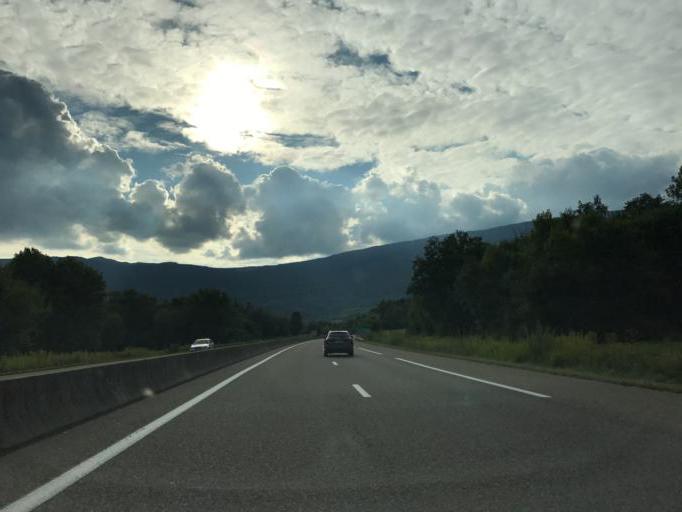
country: FR
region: Rhone-Alpes
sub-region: Departement de l'Ain
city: Peron
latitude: 46.1846
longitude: 5.9422
